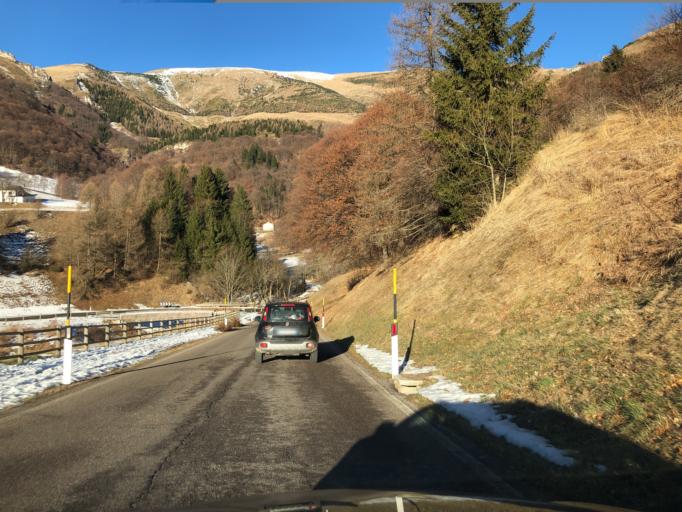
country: IT
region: Trentino-Alto Adige
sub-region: Provincia di Trento
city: Brentonico
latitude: 45.7985
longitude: 10.9152
